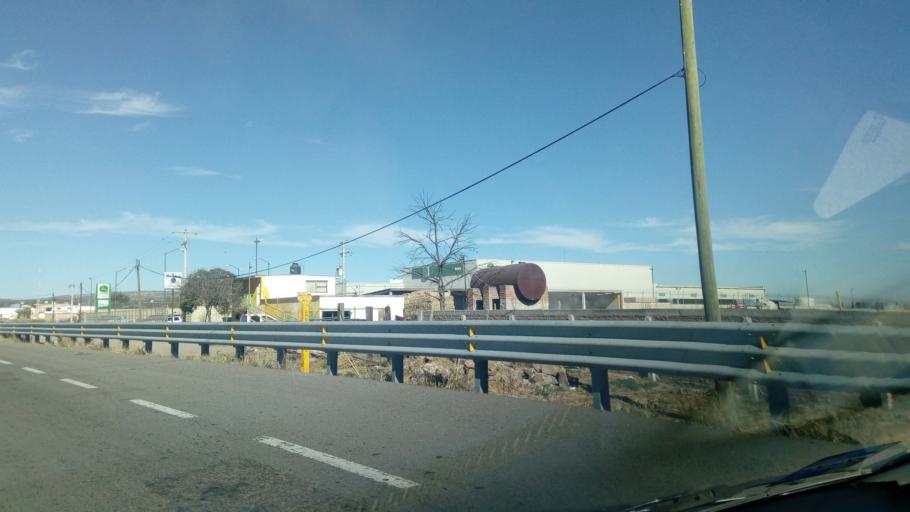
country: MX
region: Durango
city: Victoria de Durango
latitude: 24.0905
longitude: -104.5687
